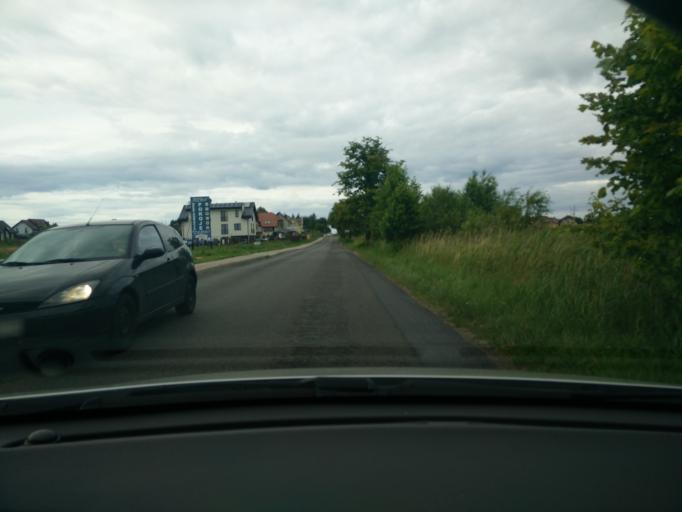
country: PL
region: Pomeranian Voivodeship
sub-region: Powiat pucki
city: Mosty
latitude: 54.6252
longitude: 18.4966
